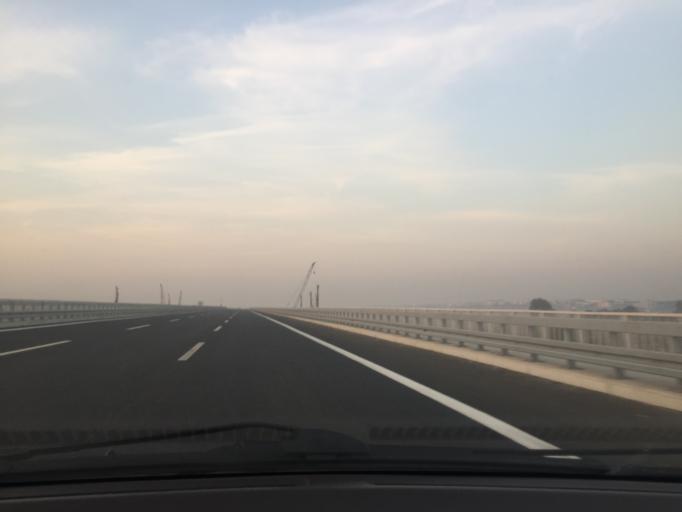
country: TR
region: Bursa
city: Karacabey
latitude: 40.2235
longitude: 28.4039
